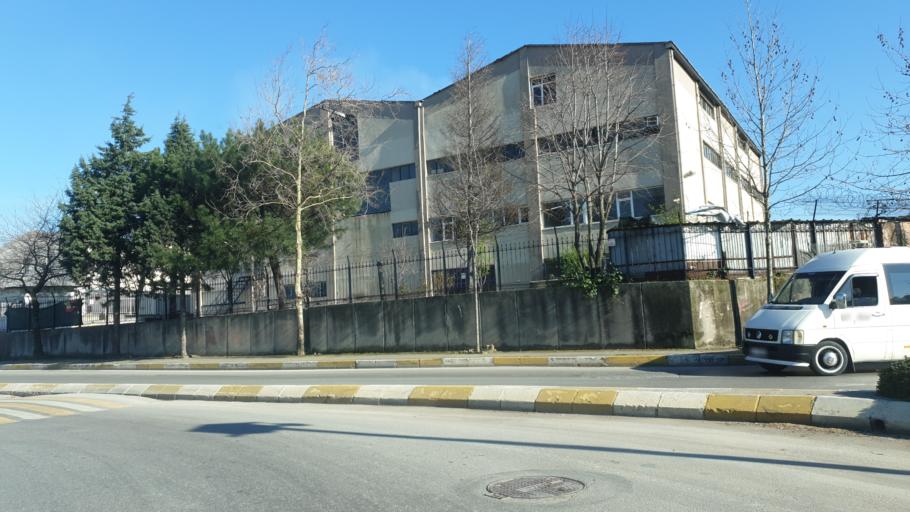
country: TR
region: Kocaeli
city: Balcik
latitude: 40.8770
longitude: 29.3654
